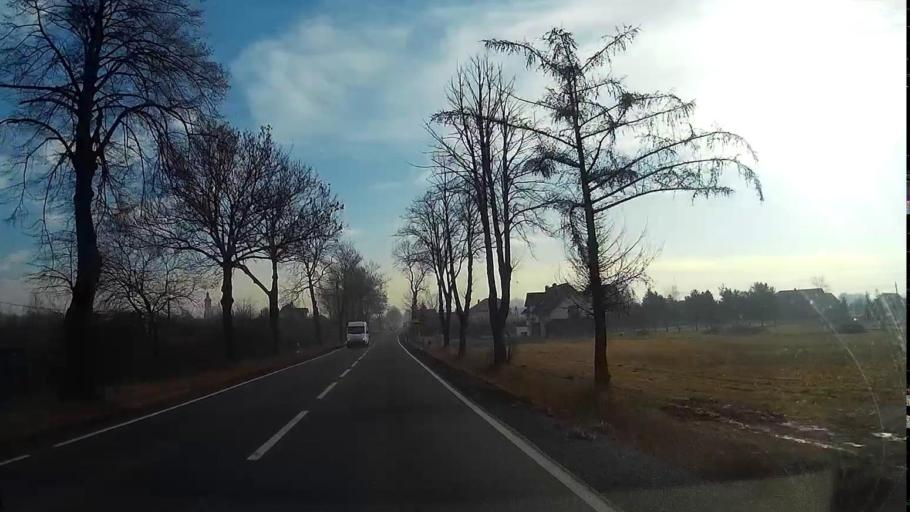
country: PL
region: Lesser Poland Voivodeship
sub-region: Powiat chrzanowski
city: Kwaczala
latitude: 50.0645
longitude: 19.4881
